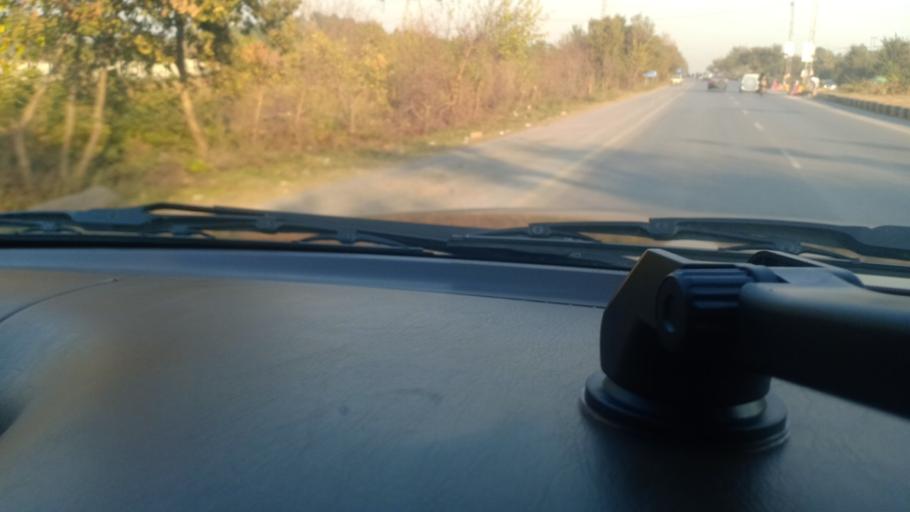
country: PK
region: Islamabad
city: Islamabad
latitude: 33.7346
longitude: 73.1573
